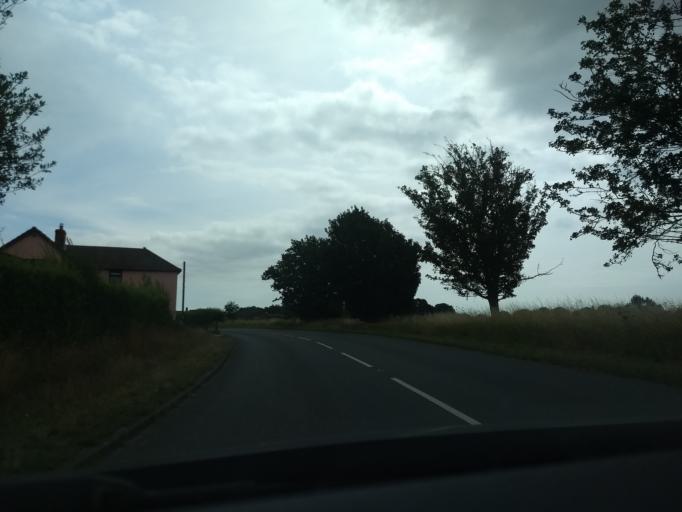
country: GB
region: England
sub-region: Suffolk
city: Shotley Gate
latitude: 51.9903
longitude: 1.2017
